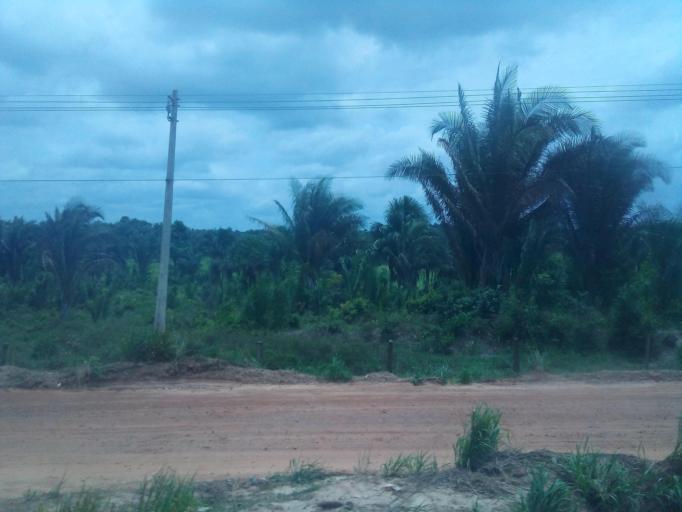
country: BR
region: Maranhao
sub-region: Santa Ines
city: Santa Ines
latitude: -3.6556
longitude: -45.7039
